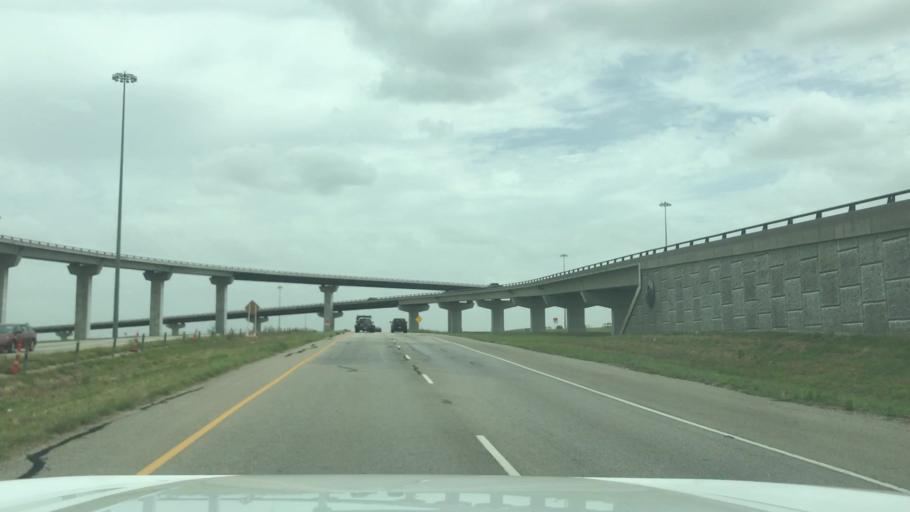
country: US
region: Texas
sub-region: McLennan County
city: Beverly Hills
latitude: 31.4946
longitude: -97.1545
